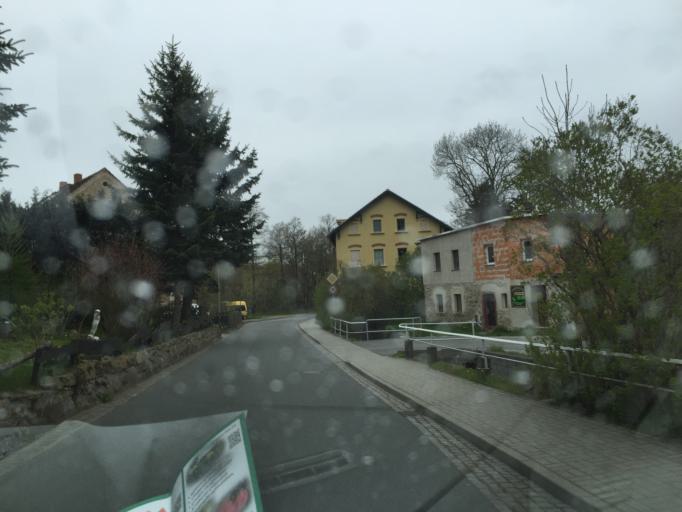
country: DE
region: Saxony
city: Lobau
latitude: 51.0821
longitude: 14.6749
